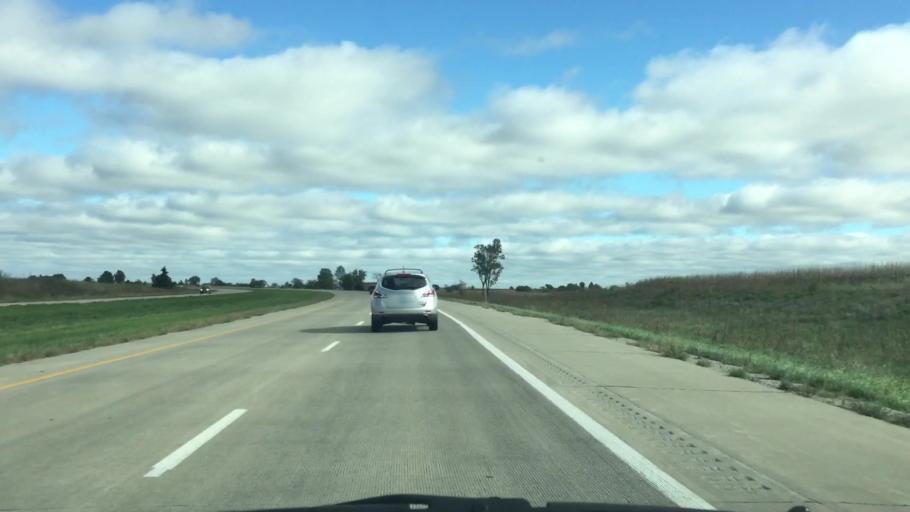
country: US
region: Iowa
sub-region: Decatur County
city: Leon
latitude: 40.8385
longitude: -93.8073
